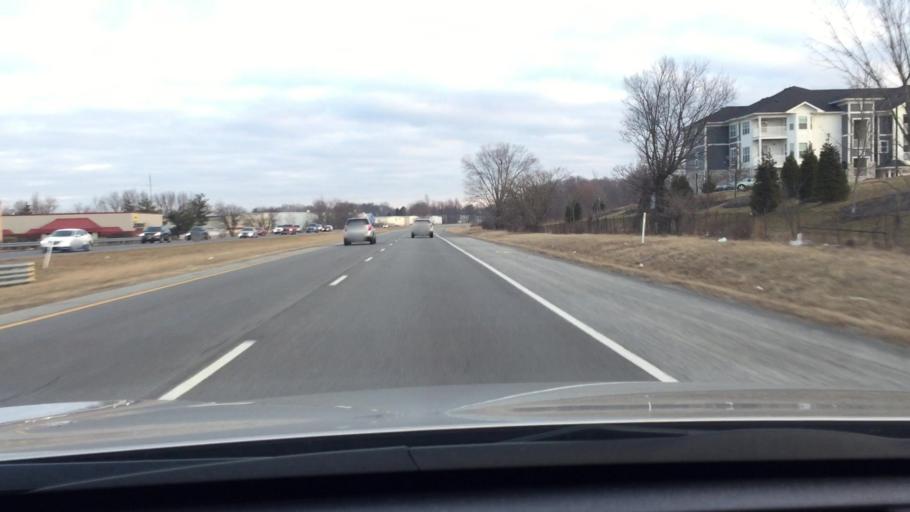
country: US
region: Indiana
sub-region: Hamilton County
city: Noblesville
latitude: 40.0065
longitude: -86.0040
